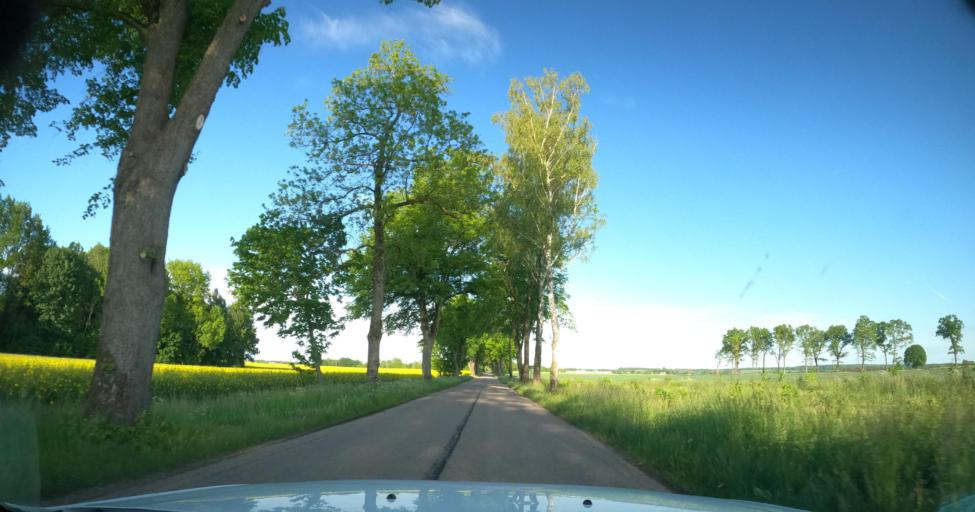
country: PL
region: Warmian-Masurian Voivodeship
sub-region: Powiat braniewski
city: Braniewo
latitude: 54.2803
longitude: 19.9045
